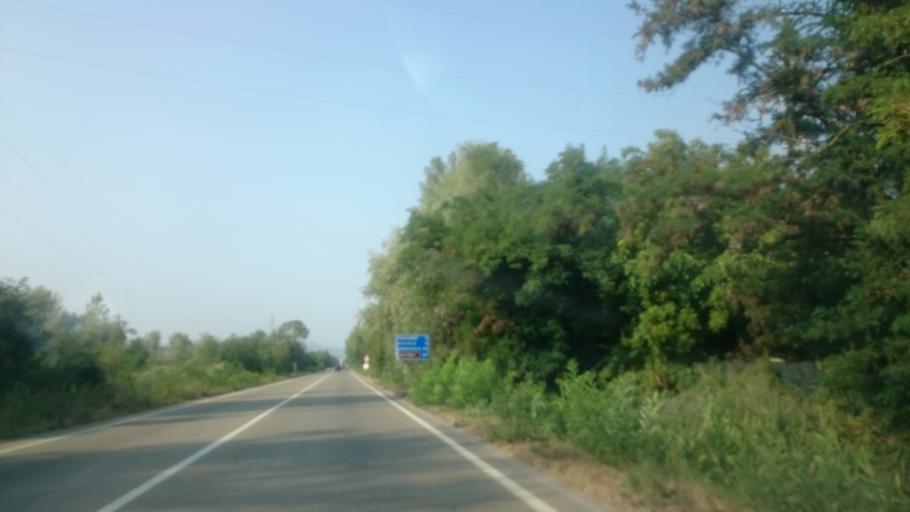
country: IT
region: Emilia-Romagna
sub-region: Provincia di Reggio Emilia
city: Veggia-Villalunga
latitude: 44.5391
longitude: 10.7619
